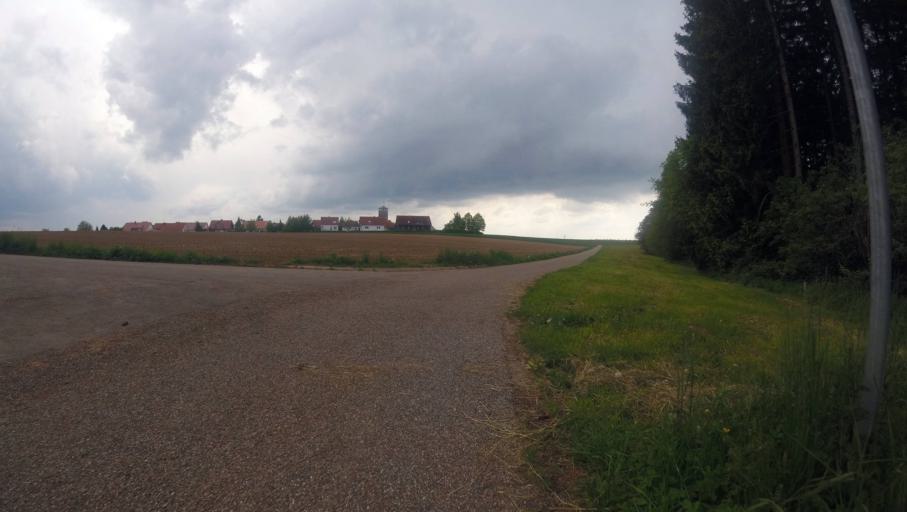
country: DE
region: Baden-Wuerttemberg
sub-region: Regierungsbezirk Stuttgart
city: Kaisersbach
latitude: 48.9350
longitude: 9.6365
